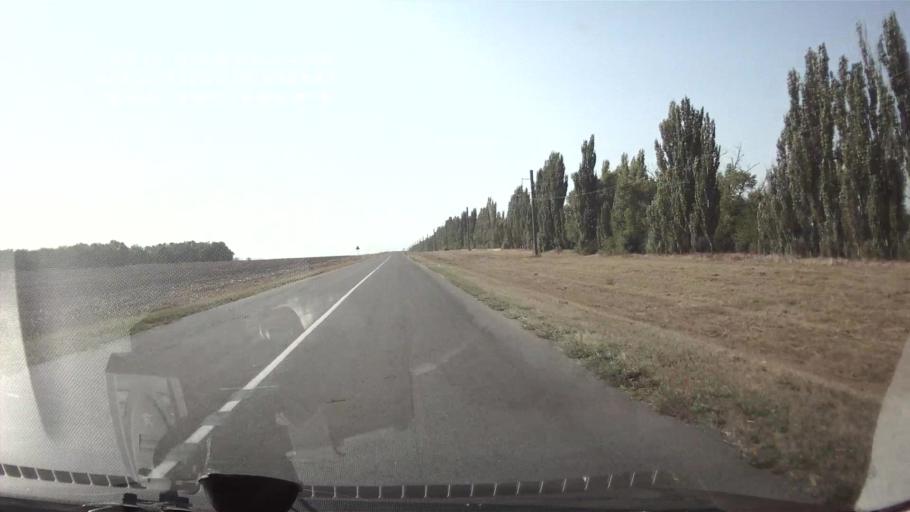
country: RU
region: Rostov
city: Tselina
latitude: 46.5256
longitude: 40.8997
